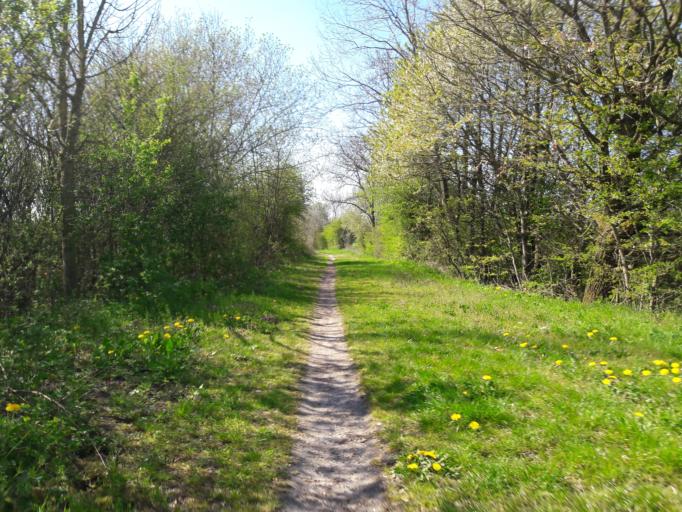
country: FR
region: Nord-Pas-de-Calais
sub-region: Departement du Nord
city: Sains-du-Nord
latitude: 50.1787
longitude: 4.0733
